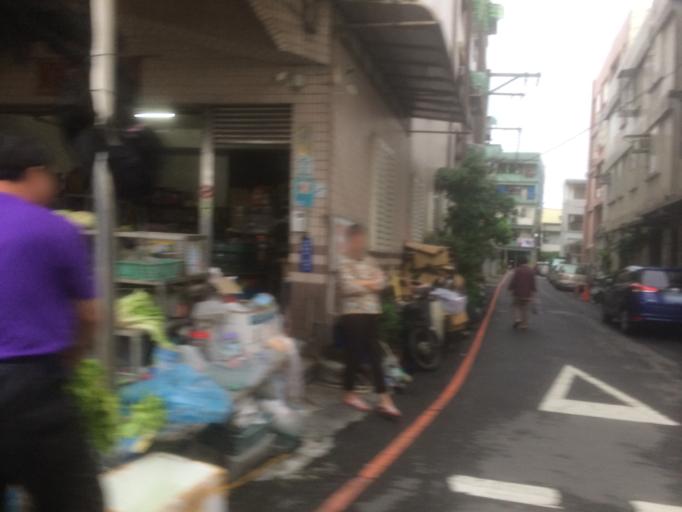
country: TW
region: Taiwan
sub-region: Yilan
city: Yilan
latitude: 24.6736
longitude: 121.7606
